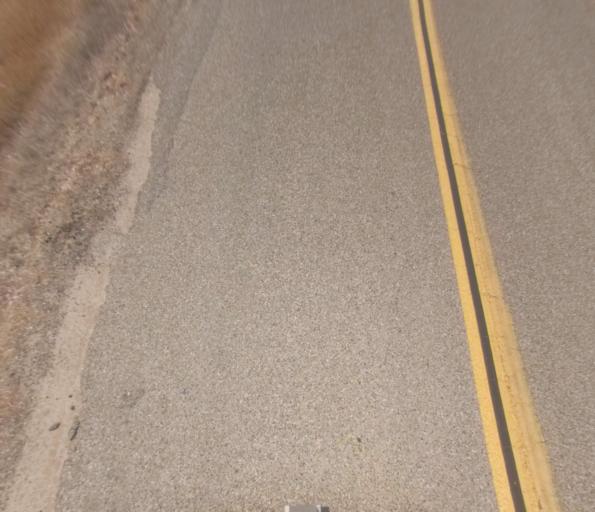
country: US
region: California
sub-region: Madera County
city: Ahwahnee
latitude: 37.3052
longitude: -119.7916
